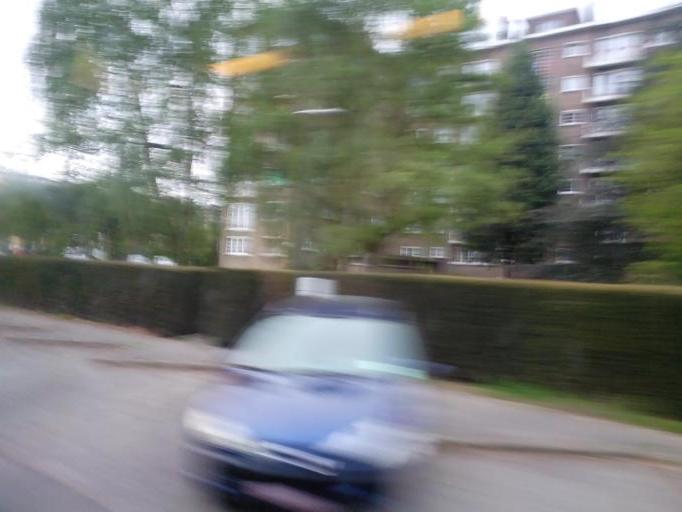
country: BE
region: Flanders
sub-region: Provincie Vlaams-Brabant
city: Diegem
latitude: 50.8749
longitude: 4.4088
